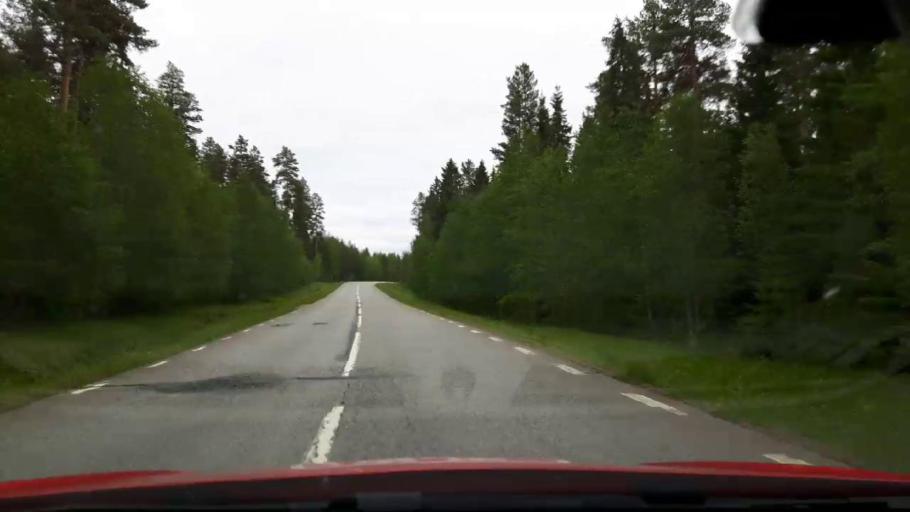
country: SE
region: Jaemtland
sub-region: Stroemsunds Kommun
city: Stroemsund
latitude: 63.3879
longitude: 15.6769
